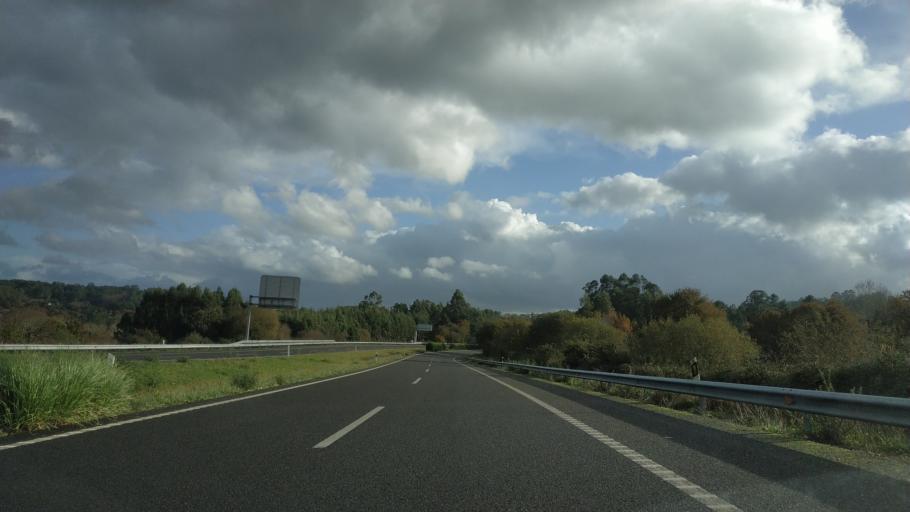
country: ES
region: Galicia
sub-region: Provincia da Coruna
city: Cambre
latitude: 43.2695
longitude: -8.3587
